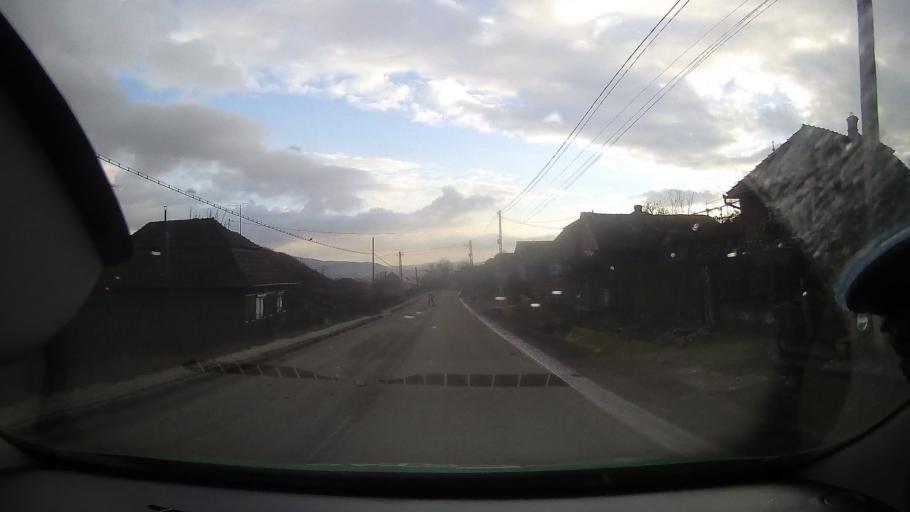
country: RO
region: Alba
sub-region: Comuna Lunca Muresului
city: Lunca Muresului
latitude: 46.4344
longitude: 23.9087
